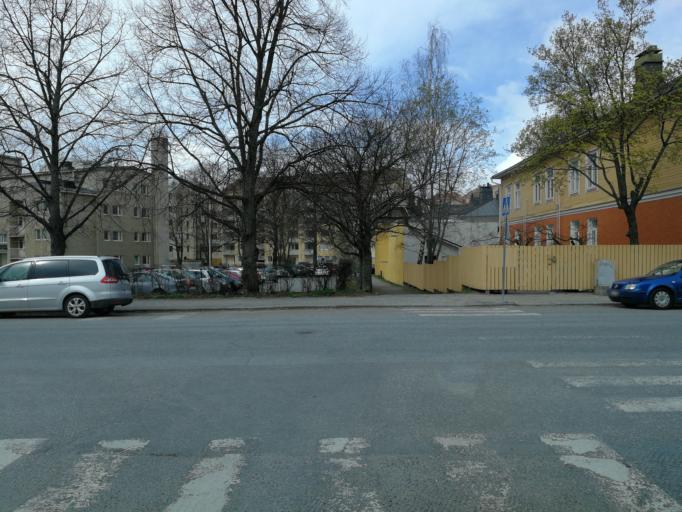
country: FI
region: Varsinais-Suomi
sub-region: Turku
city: Turku
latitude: 60.4381
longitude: 22.2613
